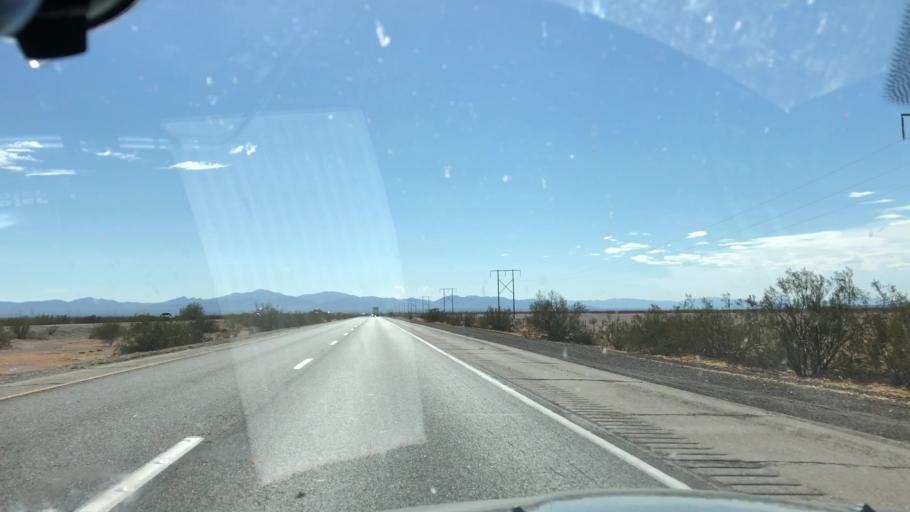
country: US
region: California
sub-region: Riverside County
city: Mesa Verde
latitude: 33.6063
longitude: -114.9307
